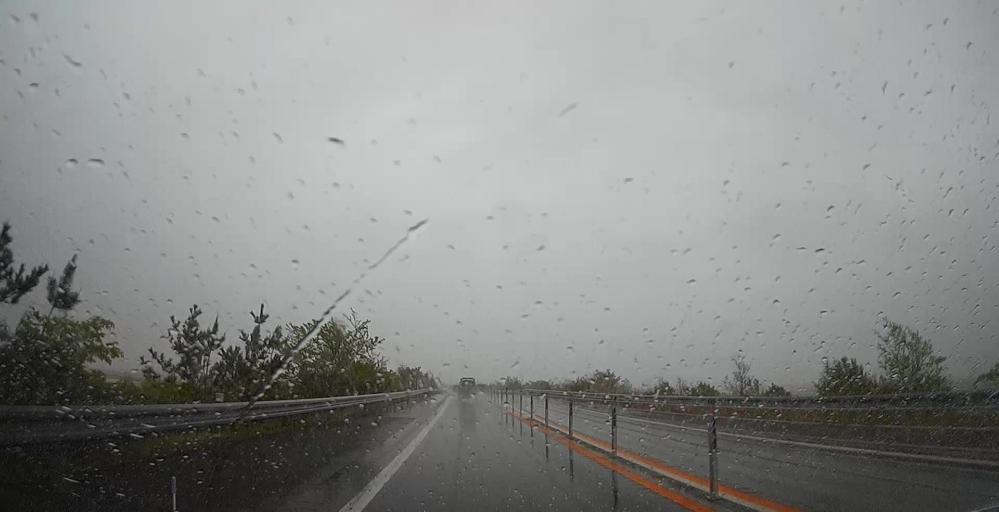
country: JP
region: Niigata
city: Shibata
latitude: 38.0036
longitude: 139.3427
